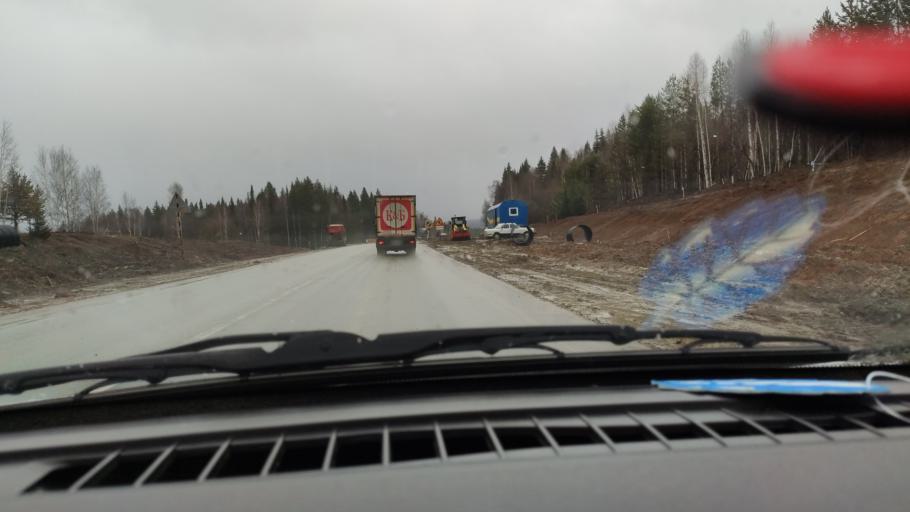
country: RU
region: Sverdlovsk
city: Bisert'
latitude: 56.8296
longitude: 59.1301
